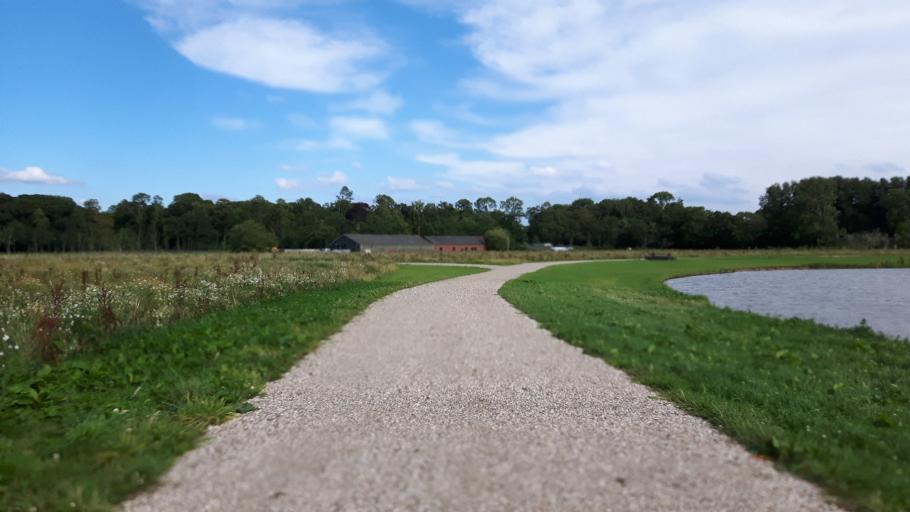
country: NL
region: Utrecht
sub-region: Stichtse Vecht
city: Spechtenkamp
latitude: 52.1238
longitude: 4.9789
